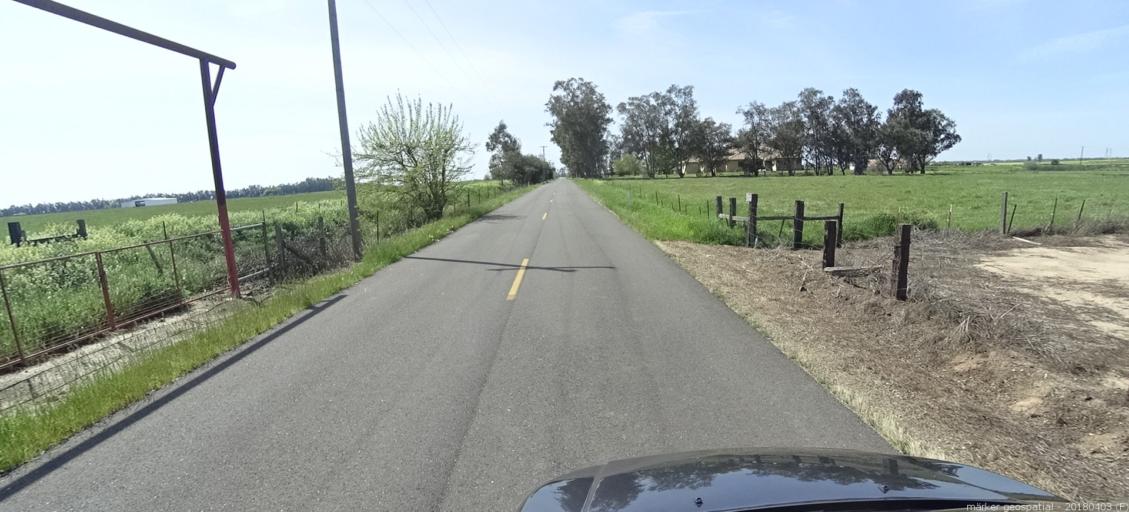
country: US
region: California
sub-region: Sacramento County
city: Herald
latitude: 38.3362
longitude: -121.2789
